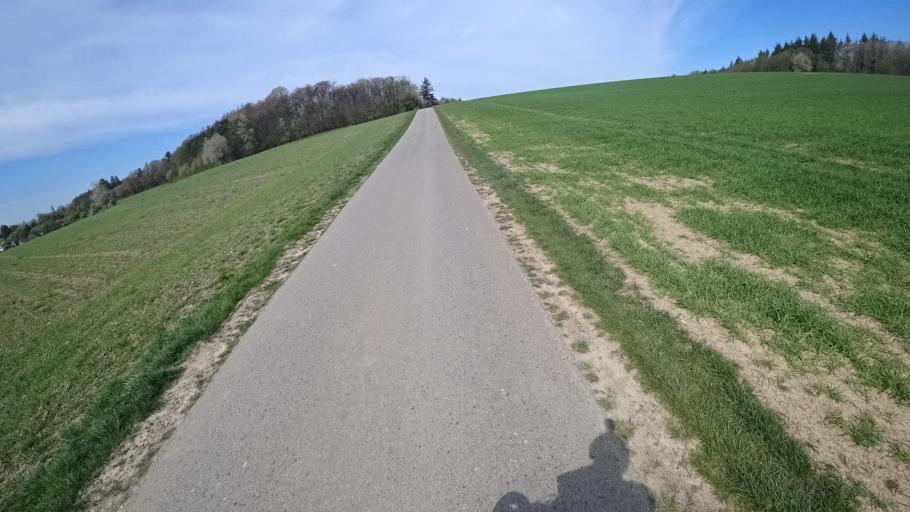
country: DE
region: Rheinland-Pfalz
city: Aach
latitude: 49.8075
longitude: 6.6083
